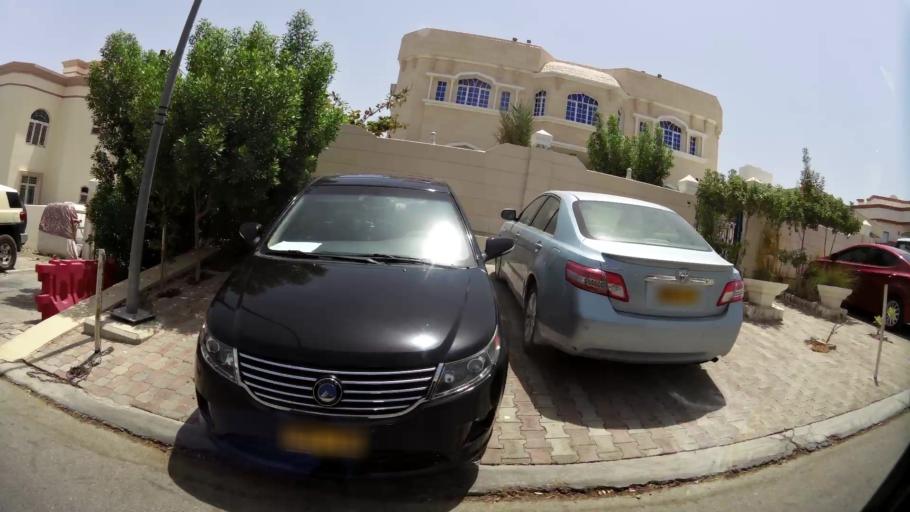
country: OM
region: Muhafazat Masqat
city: Bawshar
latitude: 23.5801
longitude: 58.4342
